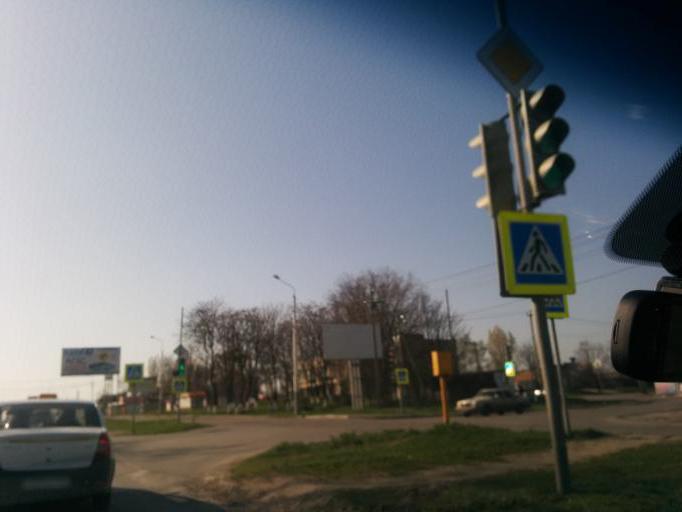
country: RU
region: Rostov
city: Shakhty
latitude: 47.7111
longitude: 40.1641
